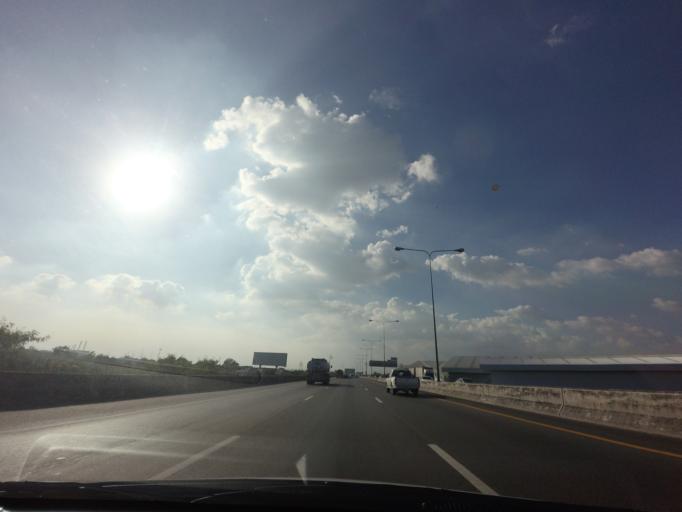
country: TH
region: Samut Prakan
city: Phra Samut Chedi
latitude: 13.6320
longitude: 100.5782
